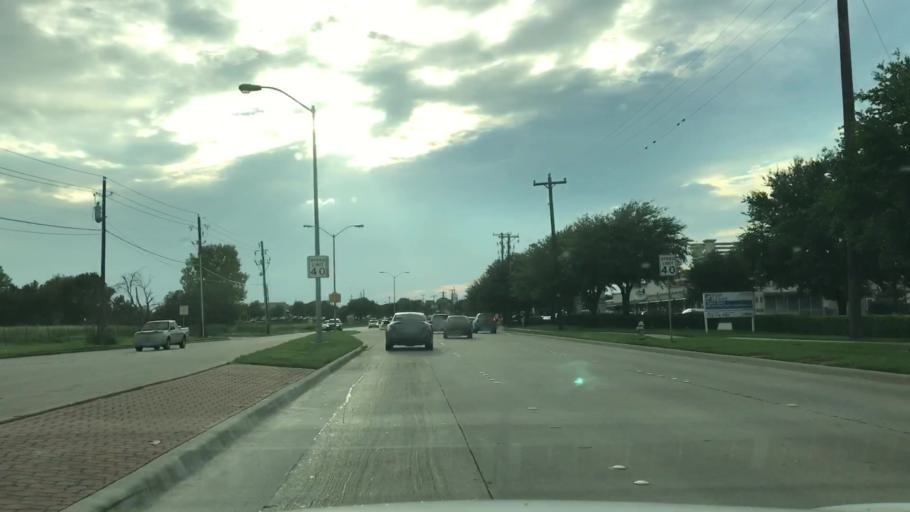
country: US
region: Texas
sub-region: Dallas County
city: Addison
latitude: 33.0276
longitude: -96.8356
